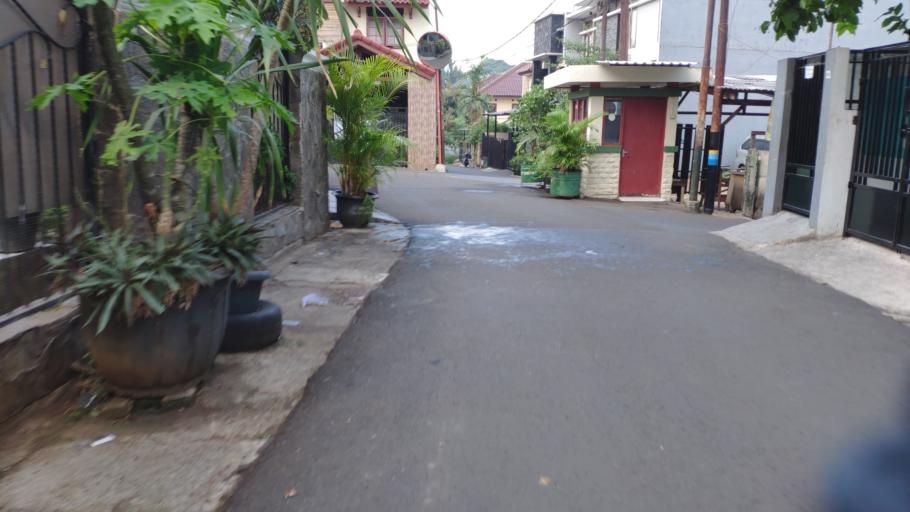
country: ID
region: Jakarta Raya
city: Jakarta
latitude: -6.2996
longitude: 106.8246
